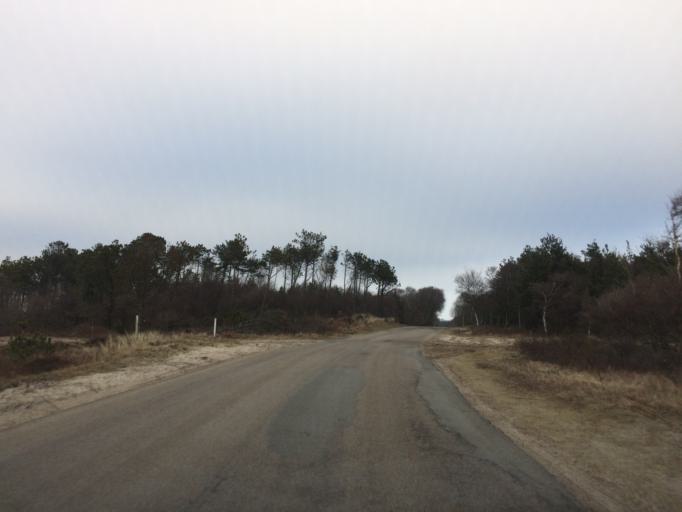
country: DK
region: South Denmark
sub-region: Varde Kommune
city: Oksbol
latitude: 55.6580
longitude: 8.1841
